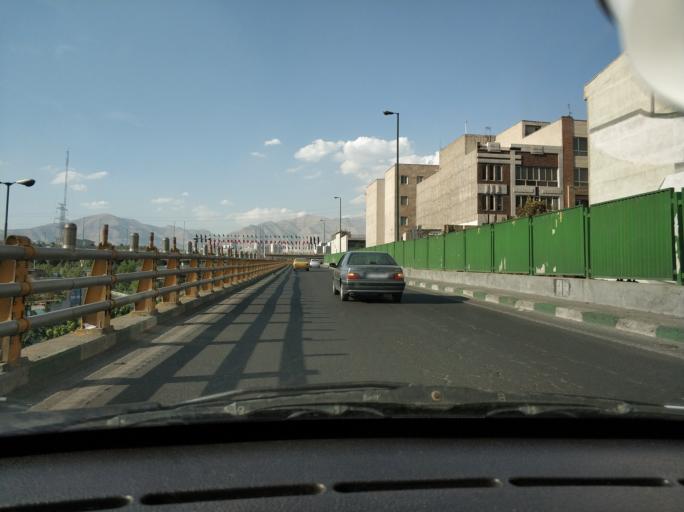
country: IR
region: Tehran
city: Tehran
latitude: 35.7377
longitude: 51.3707
